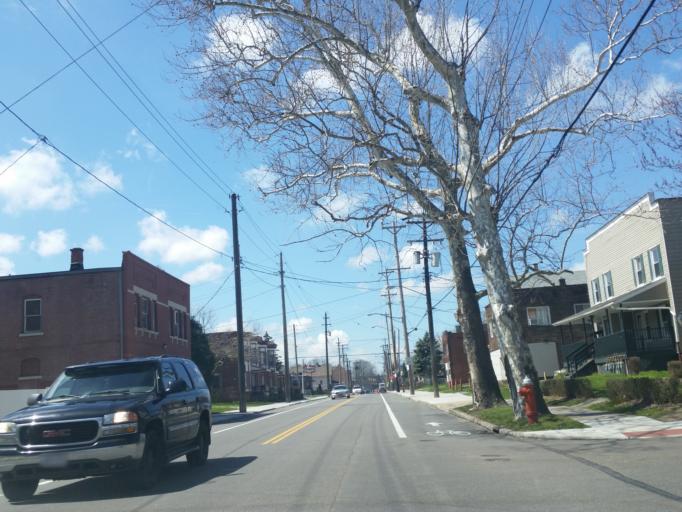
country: US
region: Ohio
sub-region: Cuyahoga County
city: Brooklyn Heights
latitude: 41.4509
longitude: -81.6977
